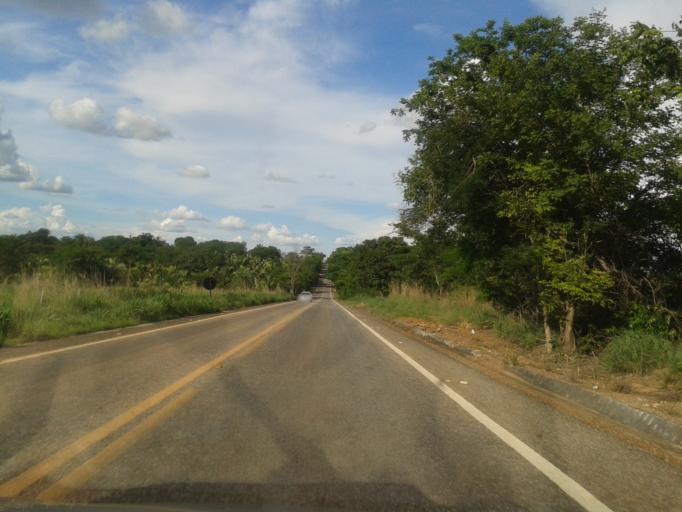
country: BR
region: Goias
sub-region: Mozarlandia
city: Mozarlandia
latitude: -14.4760
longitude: -50.4737
